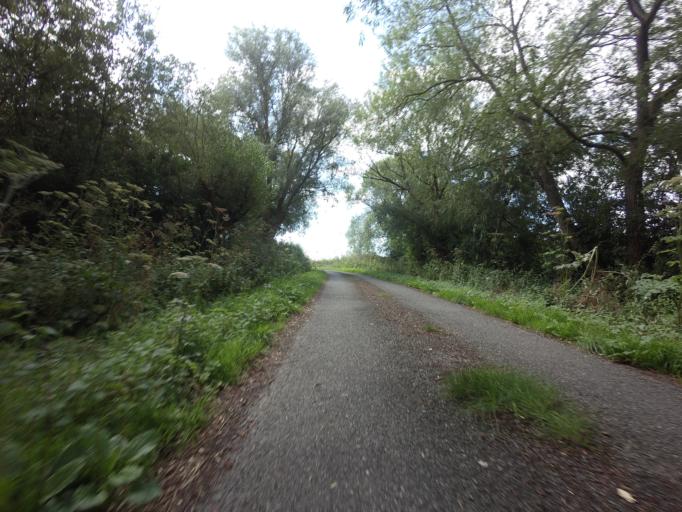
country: GB
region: England
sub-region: Kent
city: Stone
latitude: 51.0534
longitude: 0.7686
